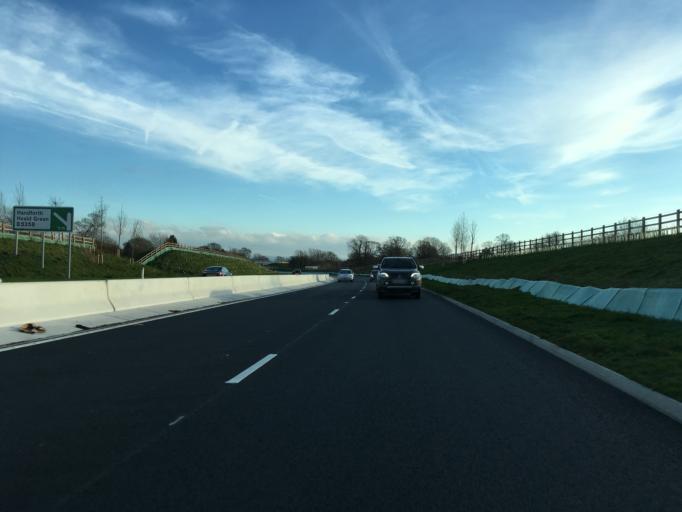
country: GB
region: England
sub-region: Cheshire East
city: Wilmslow
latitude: 53.3583
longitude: -2.2371
